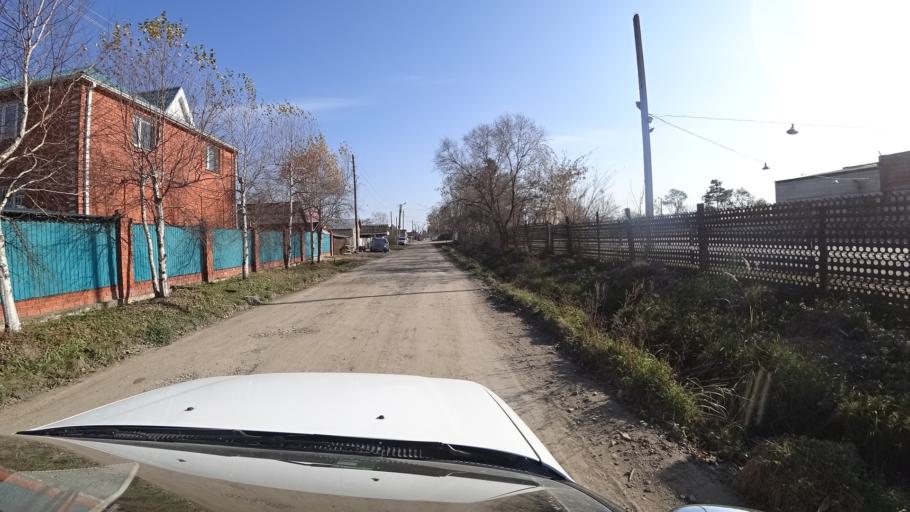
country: RU
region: Primorskiy
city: Dal'nerechensk
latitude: 45.9258
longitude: 133.7314
